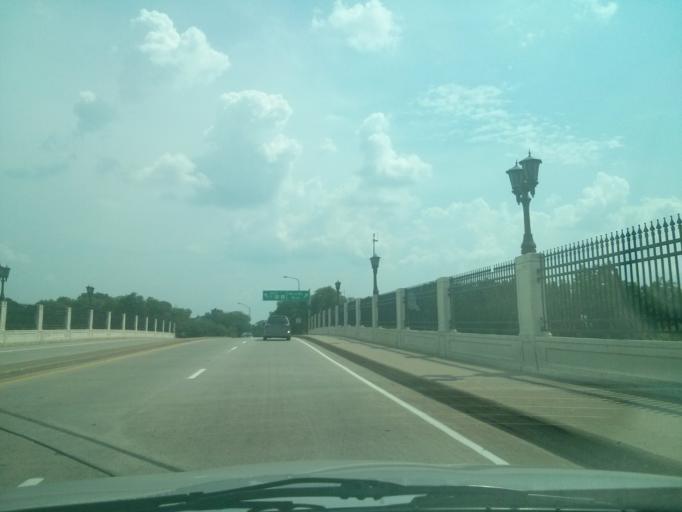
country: US
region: Minnesota
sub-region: Ramsey County
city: Saint Paul
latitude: 44.9527
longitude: -93.0702
